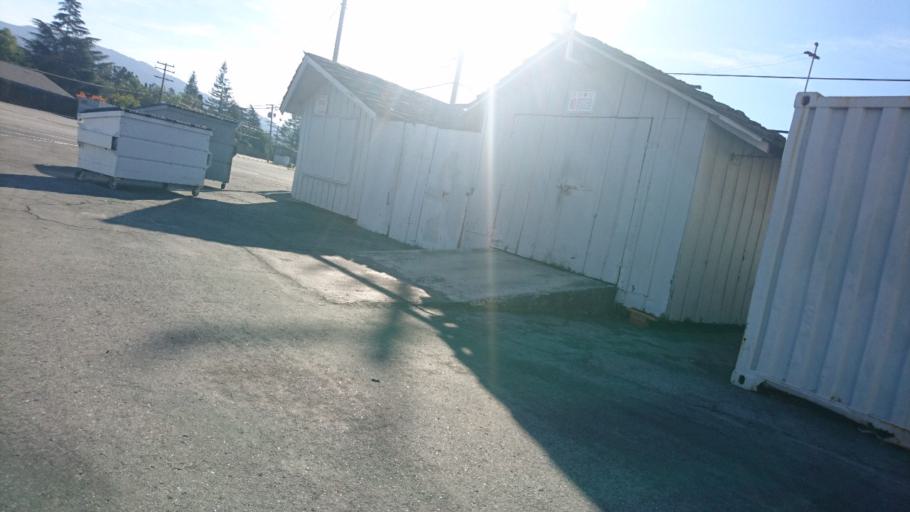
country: US
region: California
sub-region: Santa Clara County
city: Cambrian Park
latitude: 37.2599
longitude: -121.9297
